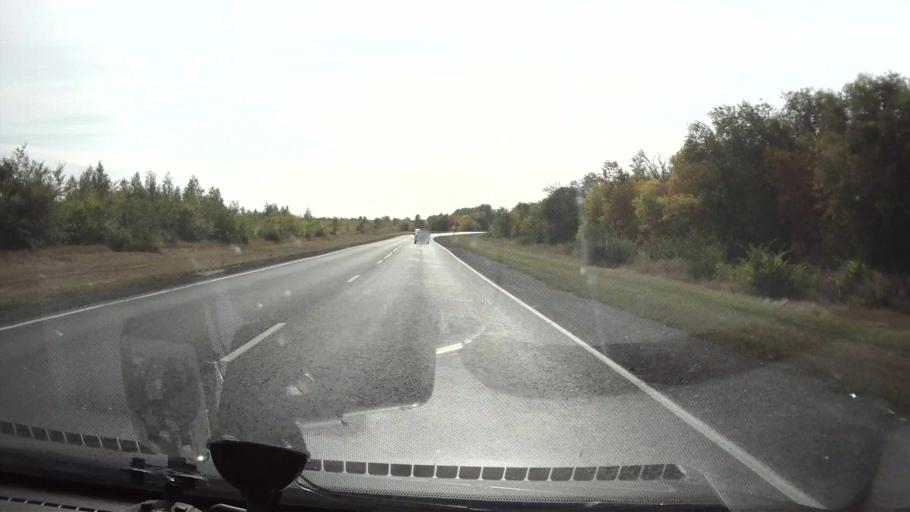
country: RU
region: Saratov
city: Balakovo
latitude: 52.1388
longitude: 47.7988
